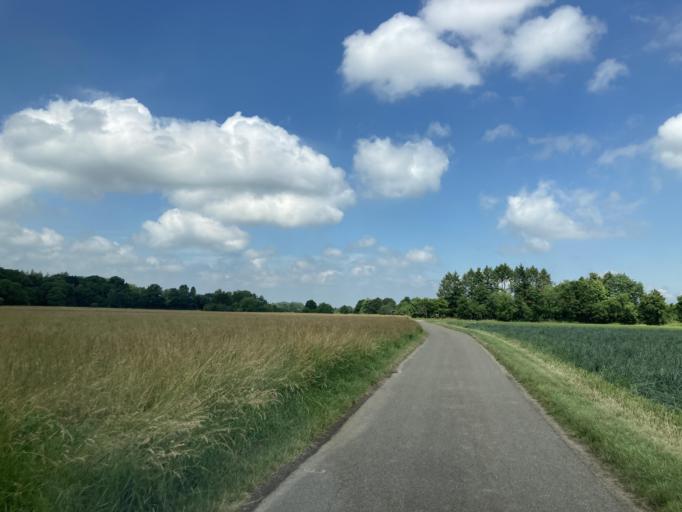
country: DE
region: Baden-Wuerttemberg
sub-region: Karlsruhe Region
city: Hambrucken
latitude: 49.1718
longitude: 8.5251
